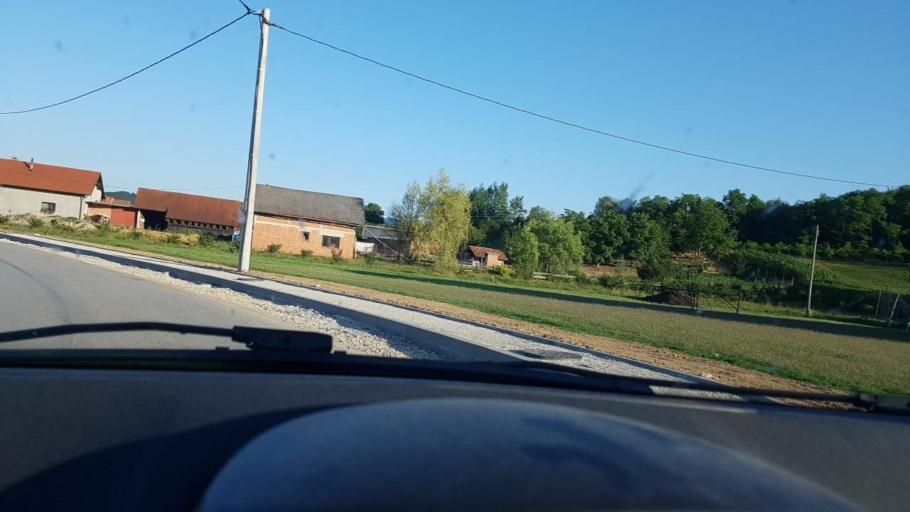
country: HR
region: Krapinsko-Zagorska
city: Bedekovcina
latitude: 46.0536
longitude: 16.0000
